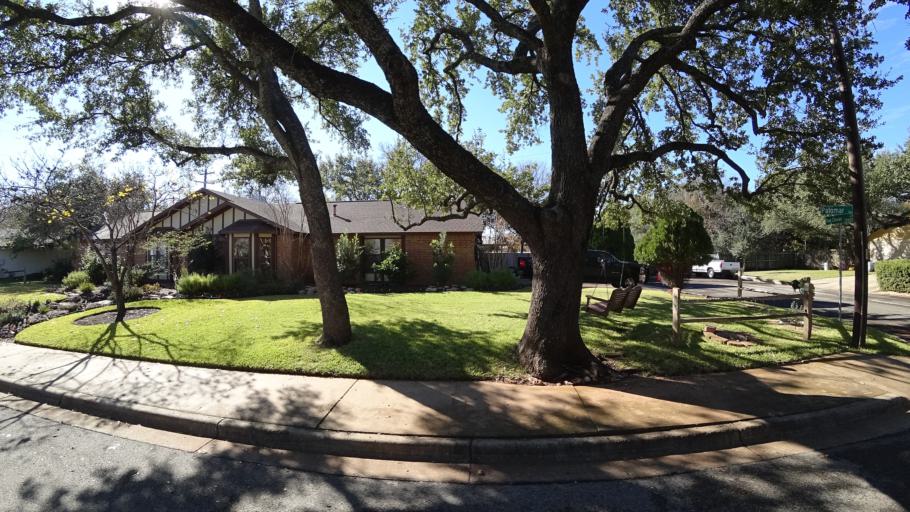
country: US
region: Texas
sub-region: Travis County
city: Wells Branch
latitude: 30.4254
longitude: -97.7104
